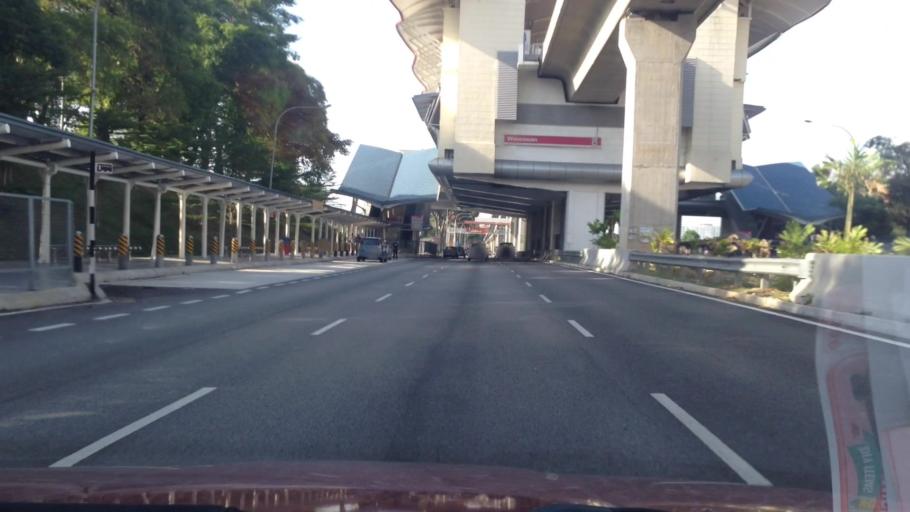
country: MY
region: Selangor
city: Subang Jaya
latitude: 3.0340
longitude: 101.5881
